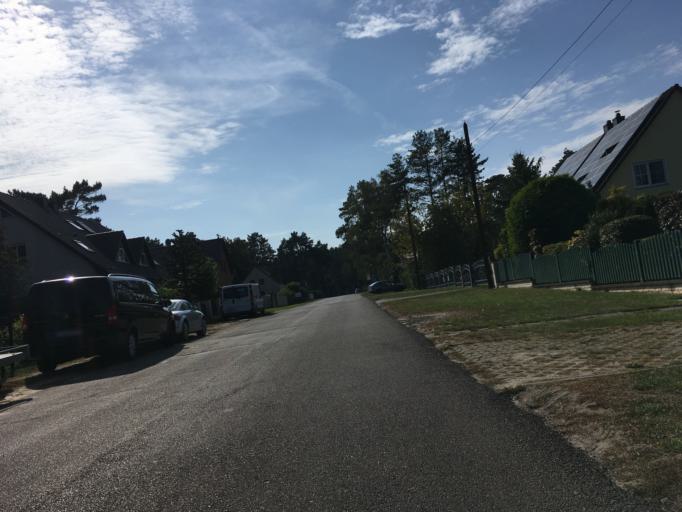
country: DE
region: Berlin
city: Muggelheim
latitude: 52.4114
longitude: 13.6497
